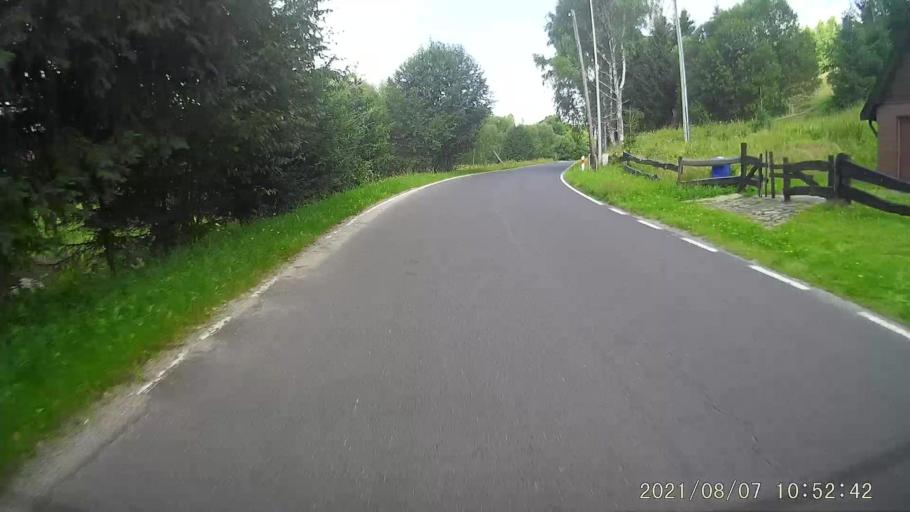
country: CZ
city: Rokytnice v Orlickych Horach
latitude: 50.2802
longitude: 16.4763
